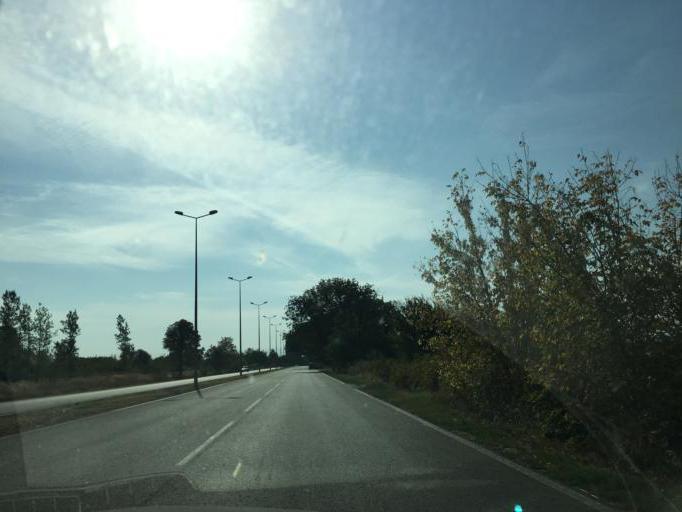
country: BG
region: Pazardzhik
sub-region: Obshtina Pazardzhik
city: Pazardzhik
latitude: 42.2197
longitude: 24.3136
